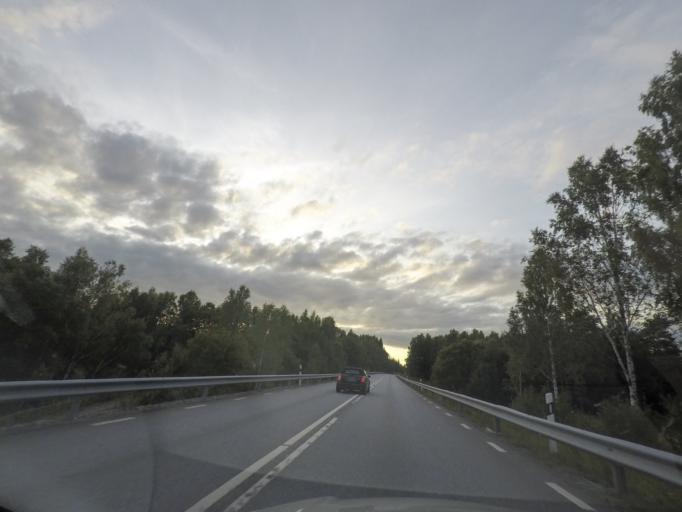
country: SE
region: OErebro
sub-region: Hallefors Kommun
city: Haellefors
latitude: 59.6631
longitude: 14.5677
